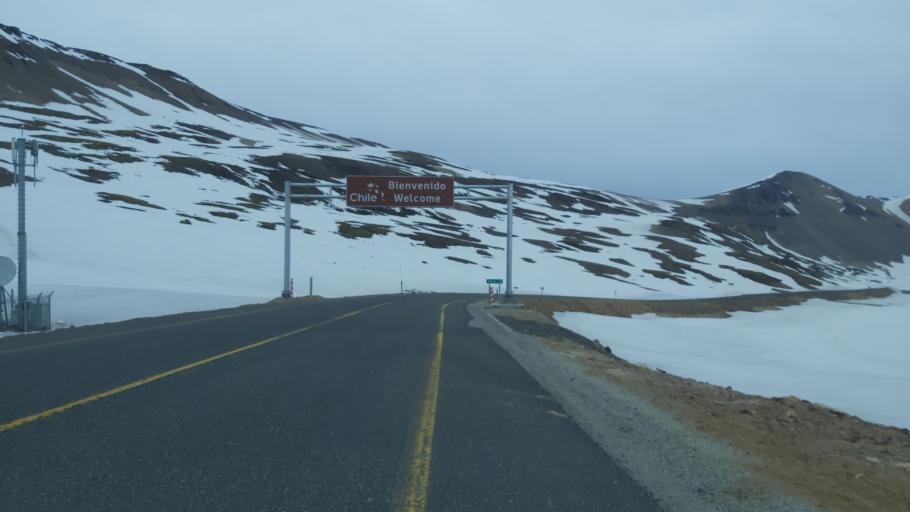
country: AR
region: Mendoza
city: Malargue
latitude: -35.9854
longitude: -70.3944
